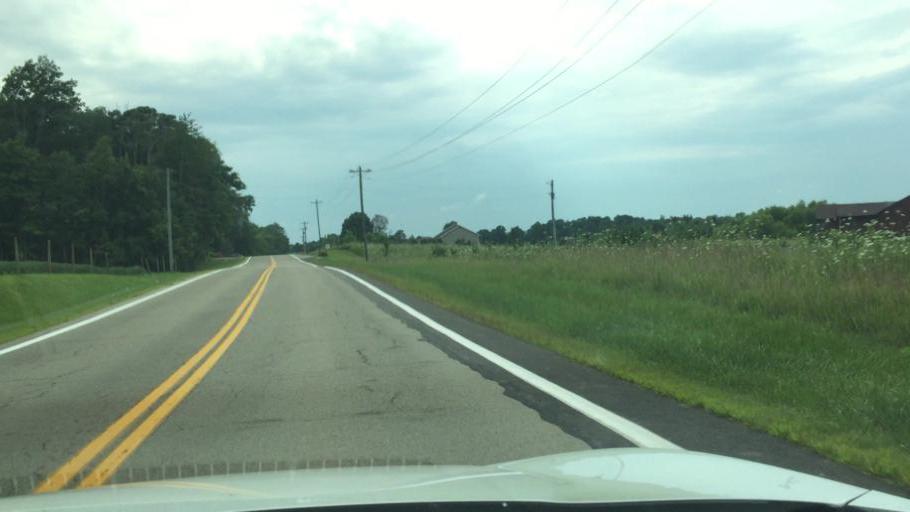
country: US
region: Ohio
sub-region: Champaign County
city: Mechanicsburg
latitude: 40.1006
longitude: -83.5624
